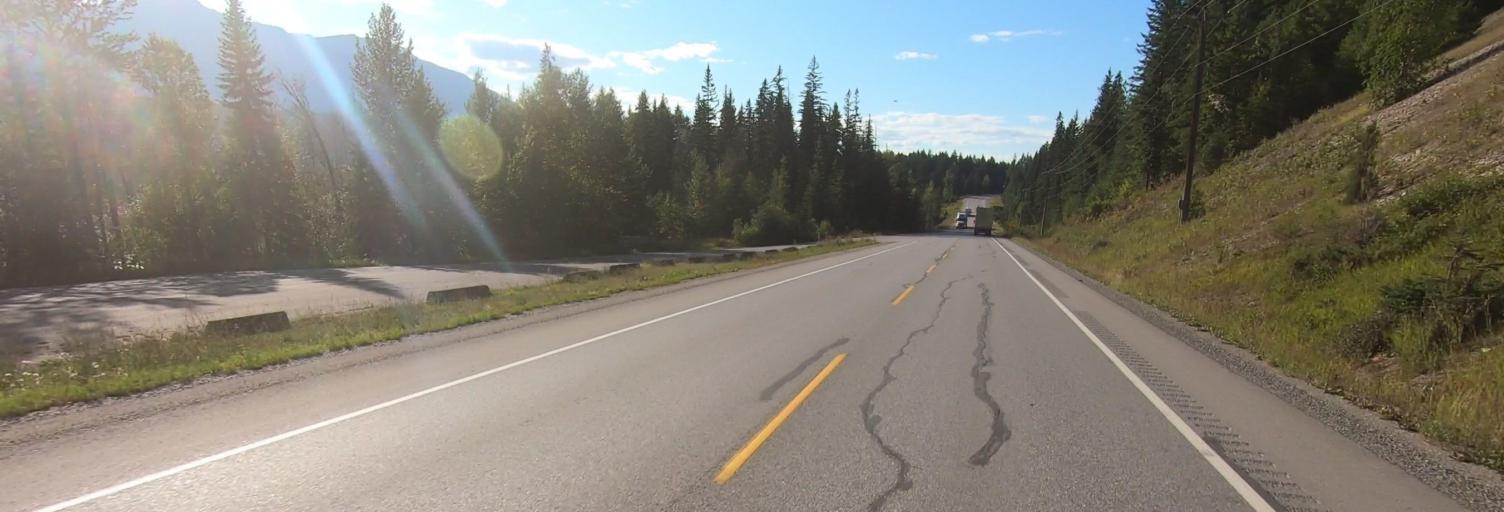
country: CA
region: British Columbia
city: Golden
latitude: 51.4430
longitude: -117.0874
